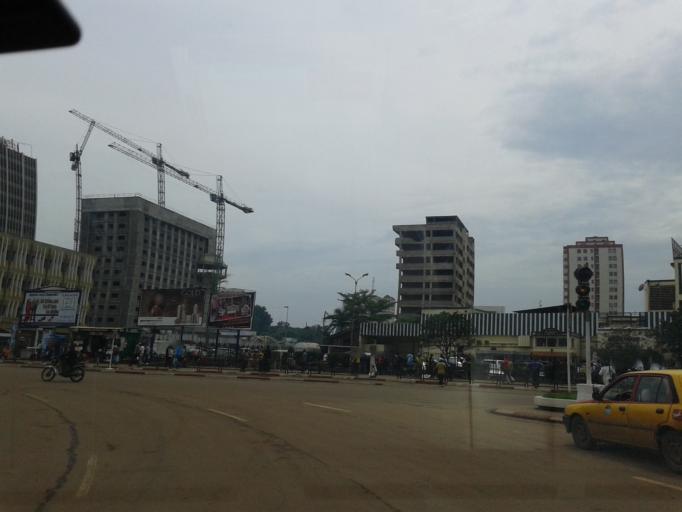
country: CM
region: Centre
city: Yaounde
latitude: 3.8620
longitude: 11.5209
